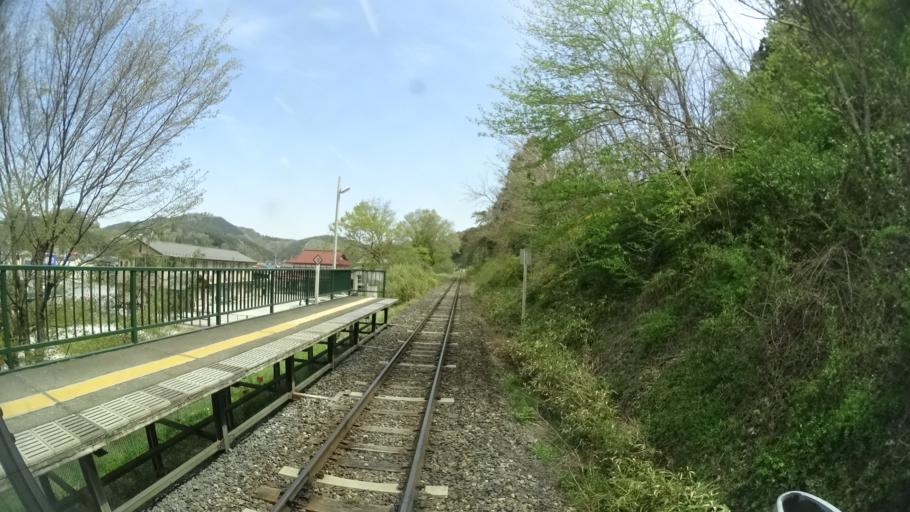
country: JP
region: Iwate
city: Ichinoseki
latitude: 38.9889
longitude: 141.2534
